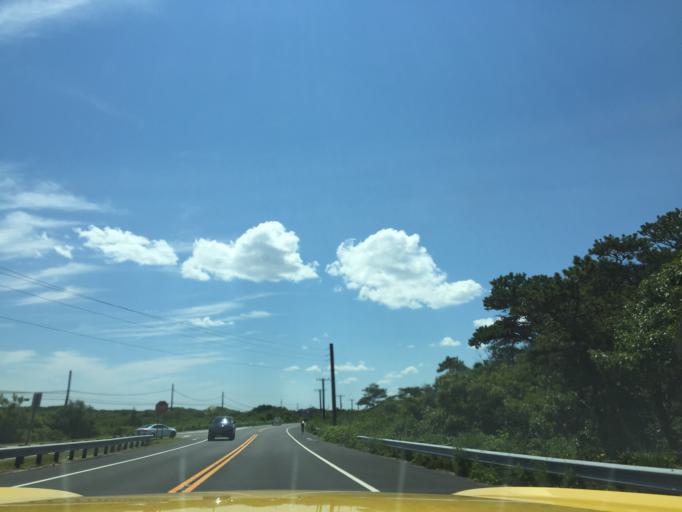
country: US
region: New York
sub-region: Suffolk County
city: Montauk
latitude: 41.0062
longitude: -72.0210
